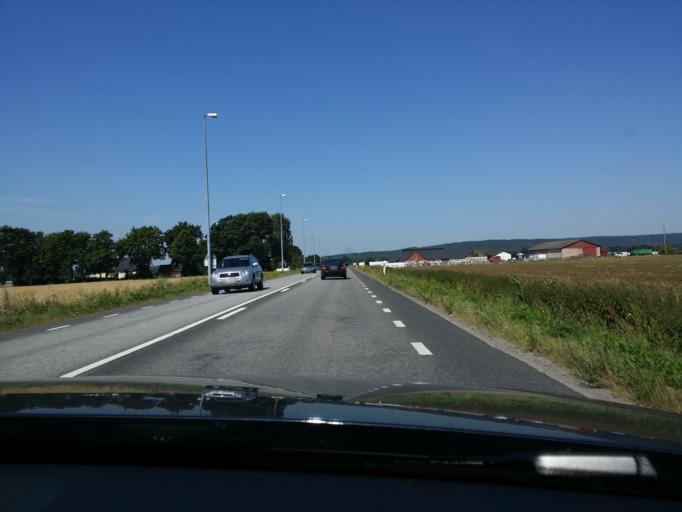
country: SE
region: Blekinge
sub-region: Solvesborgs Kommun
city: Soelvesborg
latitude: 56.0519
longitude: 14.6486
